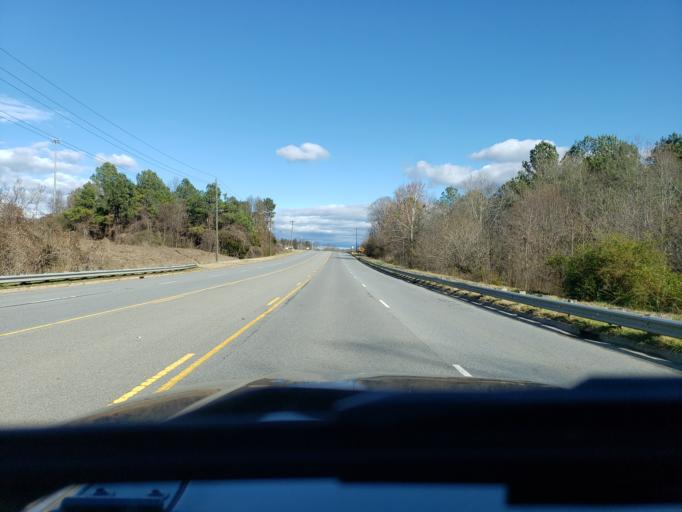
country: US
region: North Carolina
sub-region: Cleveland County
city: Shelby
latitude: 35.2581
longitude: -81.5600
